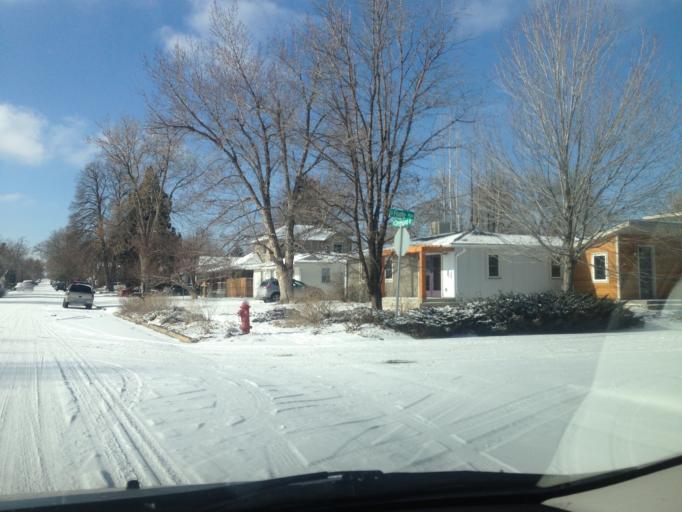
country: US
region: Colorado
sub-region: Boulder County
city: Lafayette
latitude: 39.9973
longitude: -105.0826
